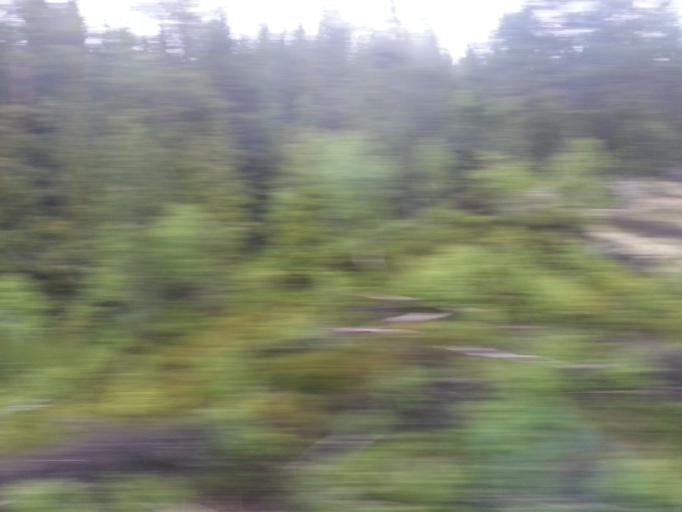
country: NO
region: Sor-Trondelag
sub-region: Rennebu
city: Berkak
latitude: 62.7815
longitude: 9.9927
